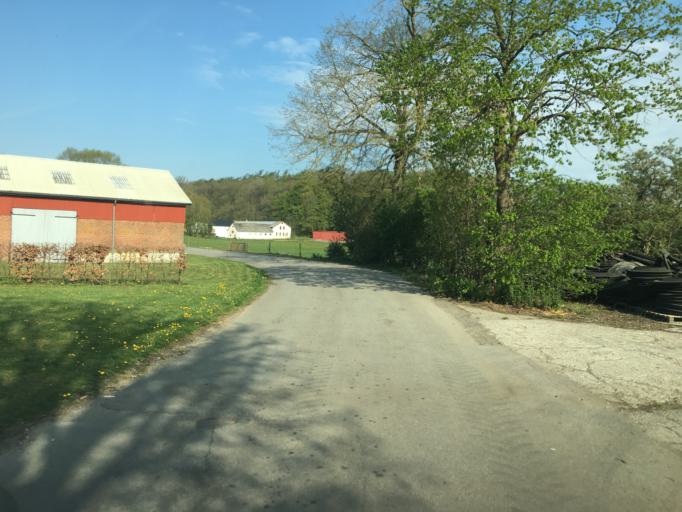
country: DK
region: South Denmark
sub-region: Haderslev Kommune
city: Vojens
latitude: 55.1872
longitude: 9.3897
